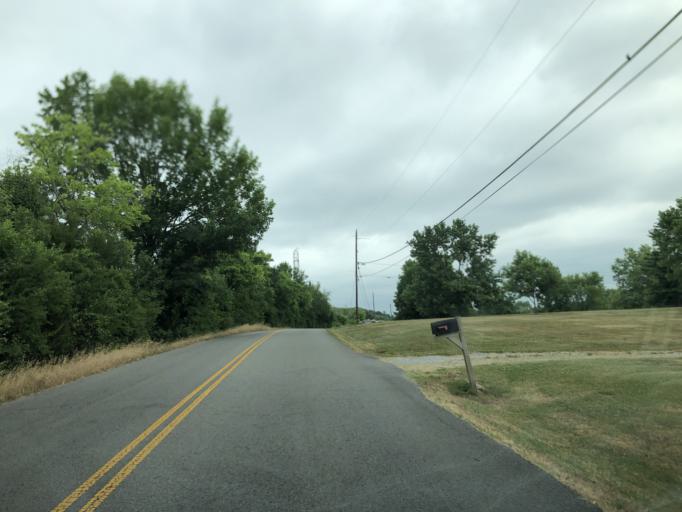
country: US
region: Tennessee
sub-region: Davidson County
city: Goodlettsville
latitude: 36.2854
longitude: -86.7314
